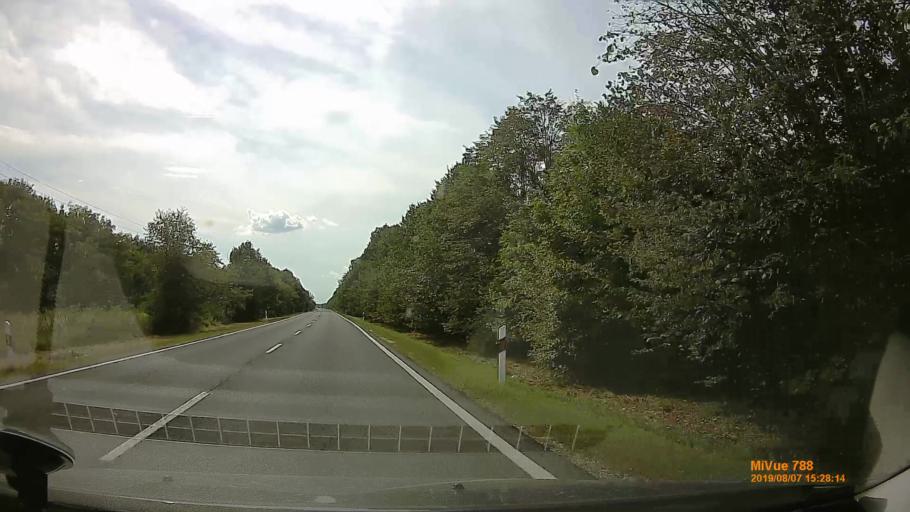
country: HU
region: Vas
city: Vep
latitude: 47.2865
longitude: 16.8036
